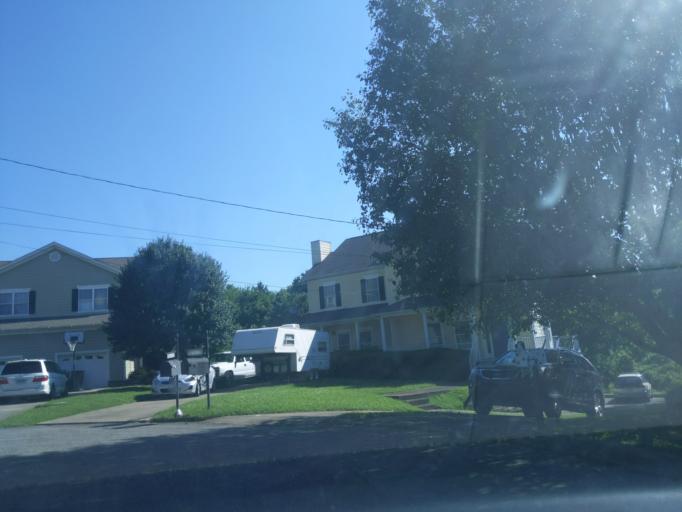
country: US
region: Tennessee
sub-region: Williamson County
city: Brentwood Estates
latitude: 36.0442
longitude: -86.7472
